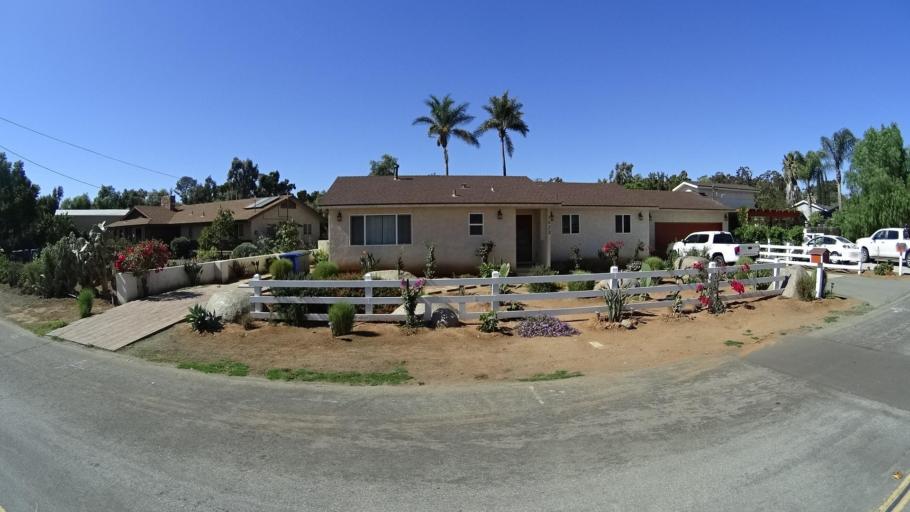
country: US
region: California
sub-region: San Diego County
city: Bonita
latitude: 32.6574
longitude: -117.0487
